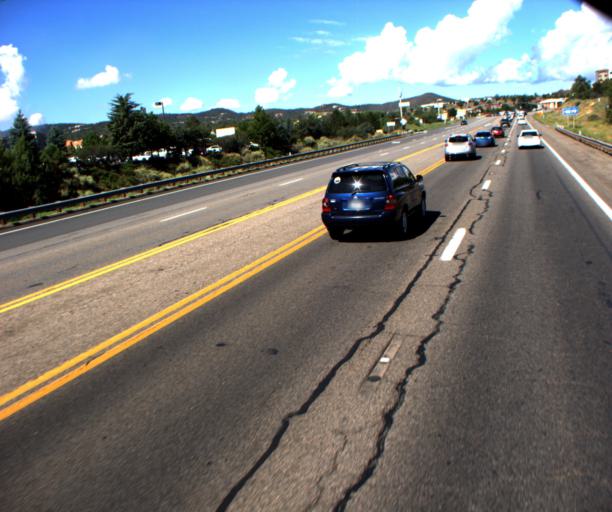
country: US
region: Arizona
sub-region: Yavapai County
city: Prescott
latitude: 34.5479
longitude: -112.3980
